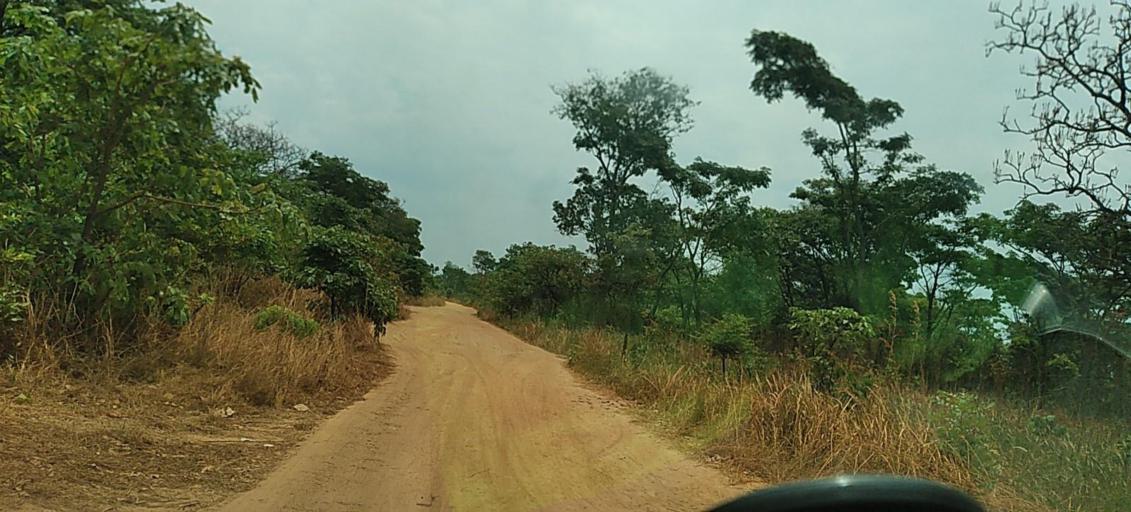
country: ZM
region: North-Western
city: Kansanshi
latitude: -12.0473
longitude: 26.3360
